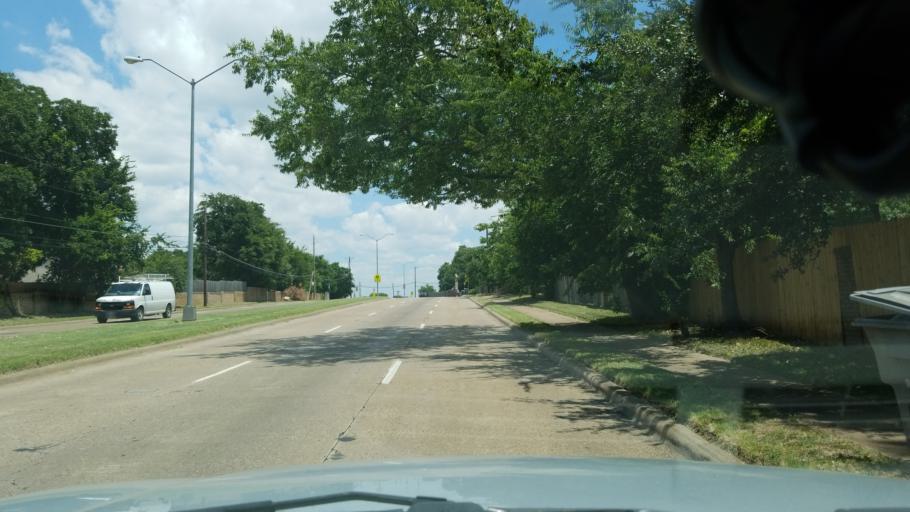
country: US
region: Texas
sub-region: Dallas County
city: Cockrell Hill
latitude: 32.6941
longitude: -96.8793
